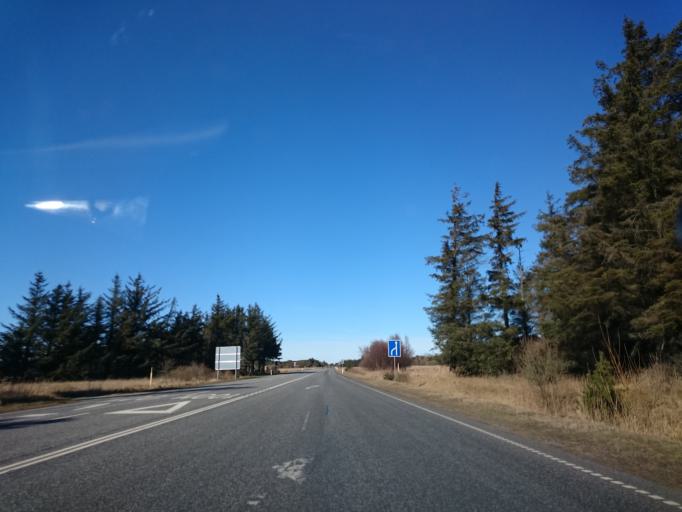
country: DK
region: North Denmark
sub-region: Frederikshavn Kommune
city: Skagen
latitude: 57.6586
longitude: 10.4573
